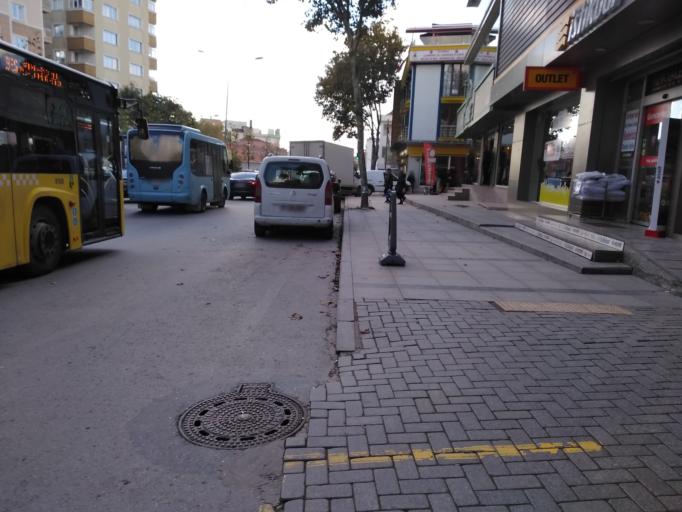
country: TR
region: Istanbul
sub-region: Atasehir
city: Atasehir
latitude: 40.9787
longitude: 29.1155
